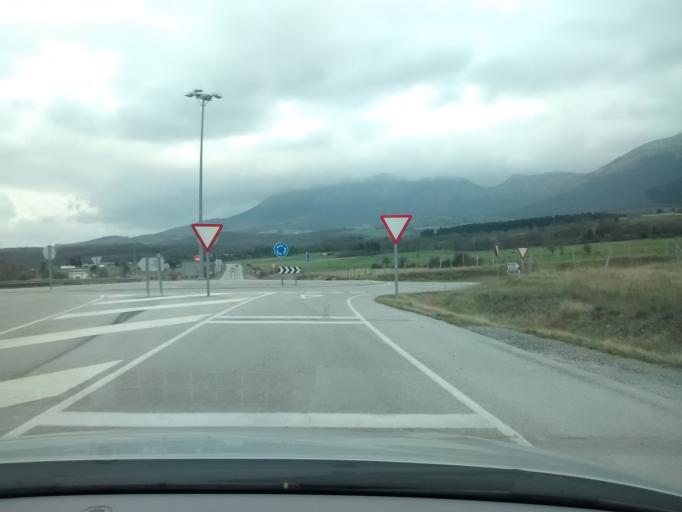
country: ES
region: Castille and Leon
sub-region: Provincia de Burgos
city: Villasana de Mena
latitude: 43.0939
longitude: -3.2904
